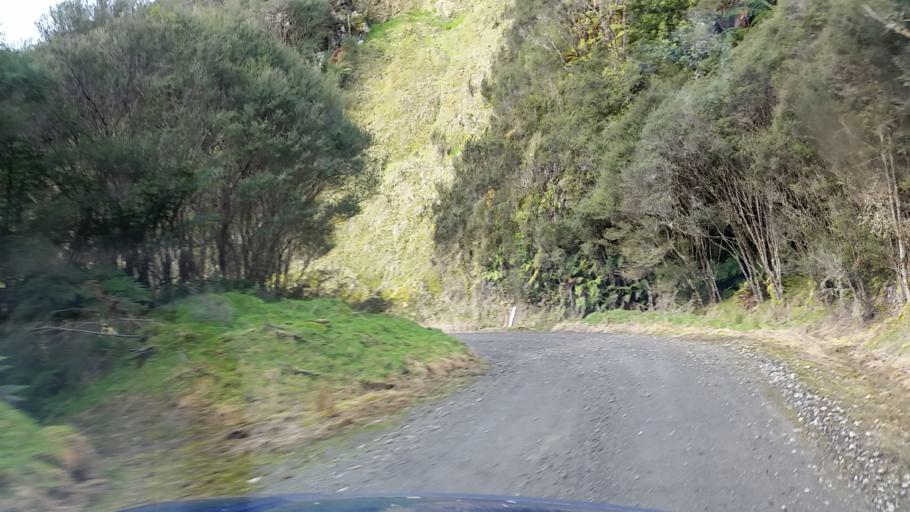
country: NZ
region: Taranaki
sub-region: South Taranaki District
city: Eltham
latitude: -39.2660
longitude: 174.7719
